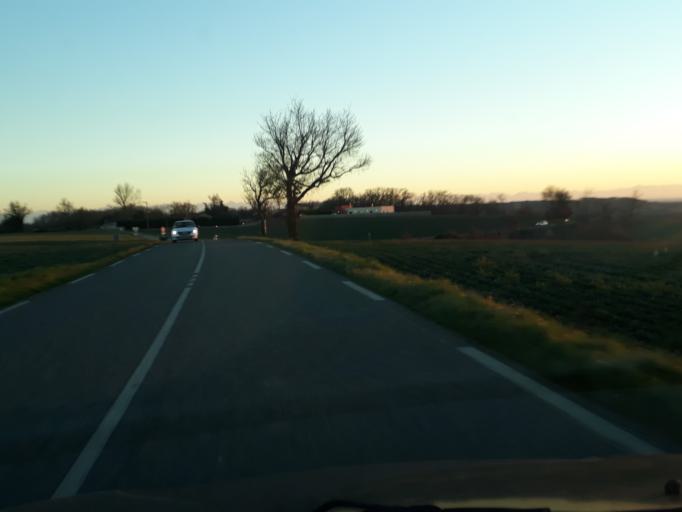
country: FR
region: Midi-Pyrenees
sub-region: Departement du Gers
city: Pujaudran
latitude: 43.5787
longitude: 1.1315
